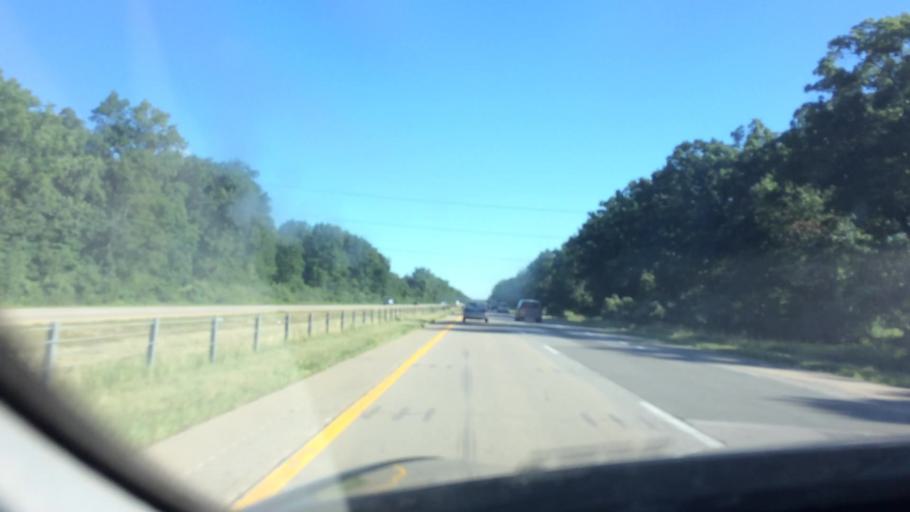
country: US
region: Michigan
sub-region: Monroe County
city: Petersburg
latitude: 41.8590
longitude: -83.6608
